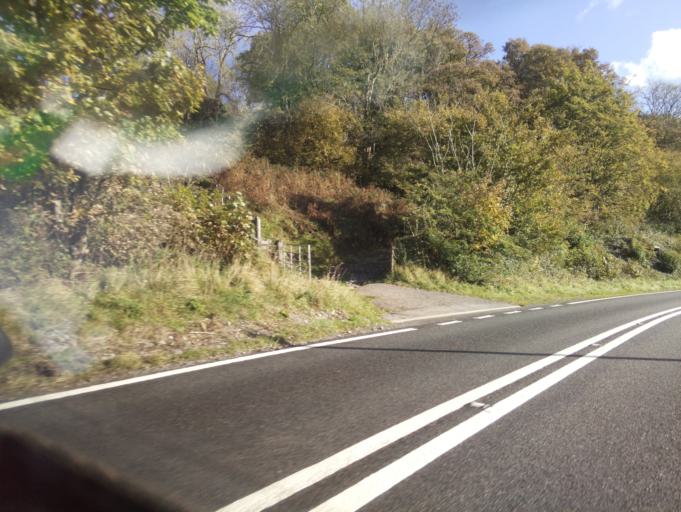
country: GB
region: Wales
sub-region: Merthyr Tydfil County Borough
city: Merthyr Tydfil
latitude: 51.7882
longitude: -3.4263
